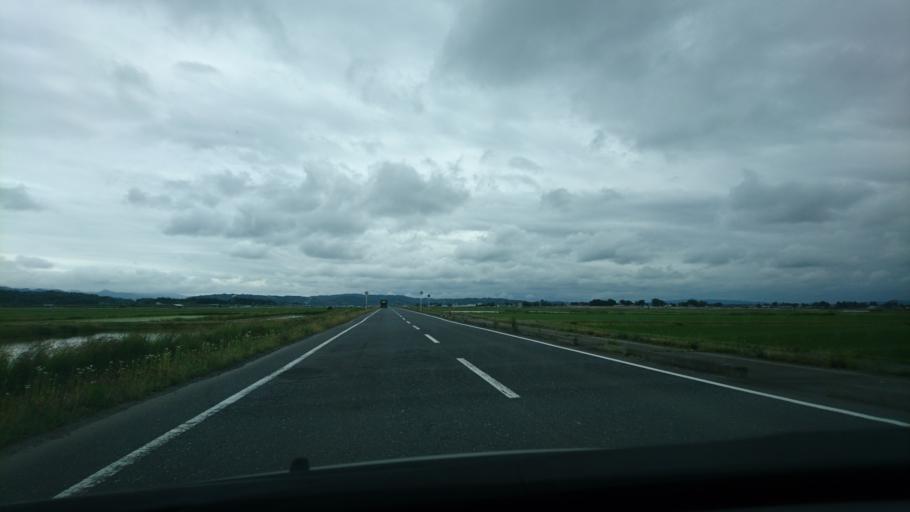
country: JP
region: Miyagi
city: Wakuya
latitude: 38.6887
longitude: 141.2608
